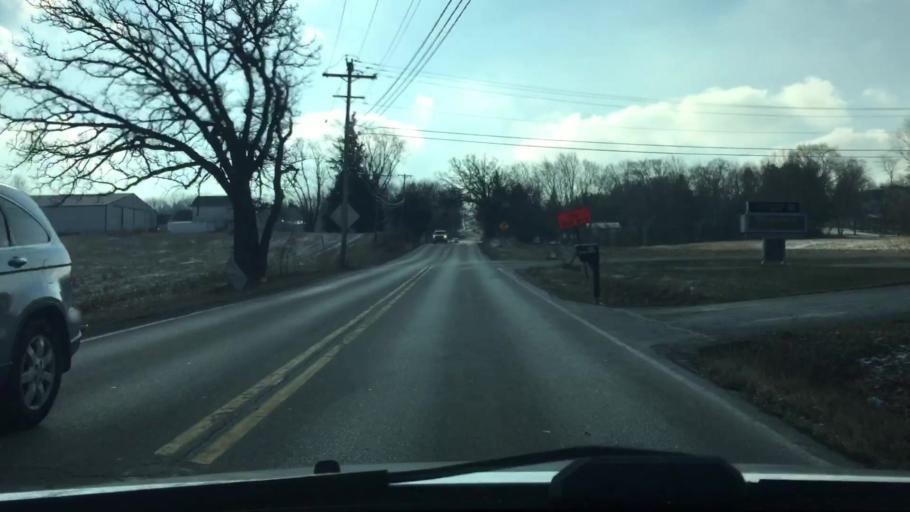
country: US
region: Wisconsin
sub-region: Waukesha County
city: Waukesha
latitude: 42.9917
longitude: -88.2892
